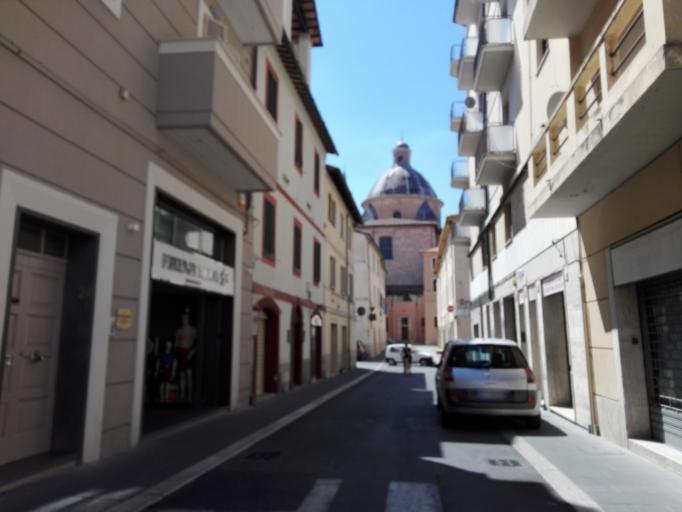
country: IT
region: Umbria
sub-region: Provincia di Perugia
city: Foligno
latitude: 42.9576
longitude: 12.7045
